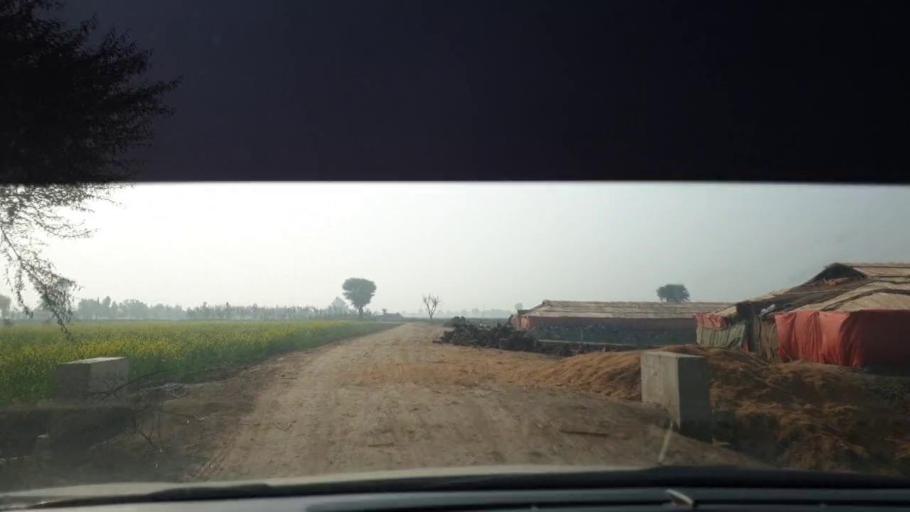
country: PK
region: Sindh
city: Berani
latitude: 25.7809
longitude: 68.7977
